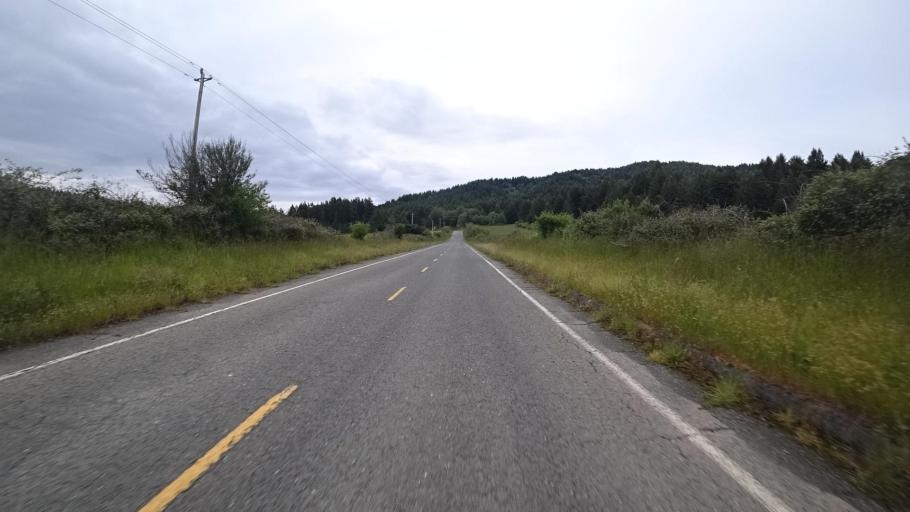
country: US
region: California
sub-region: Humboldt County
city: Blue Lake
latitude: 40.8615
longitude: -123.9957
